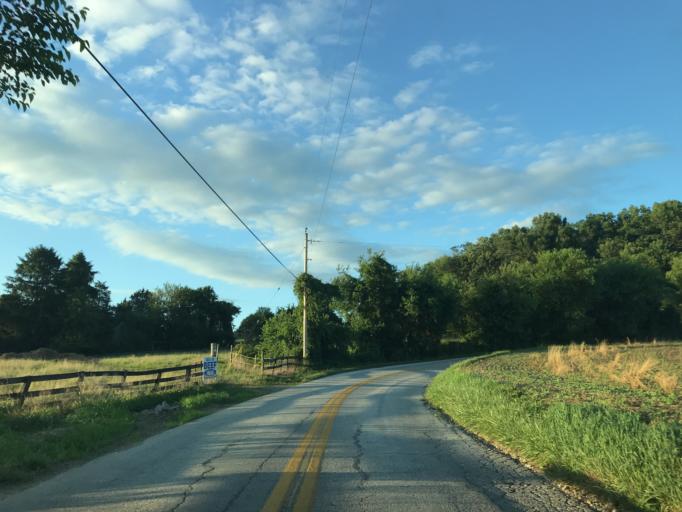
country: US
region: Maryland
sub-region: Baltimore County
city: Hunt Valley
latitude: 39.5652
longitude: -76.6898
